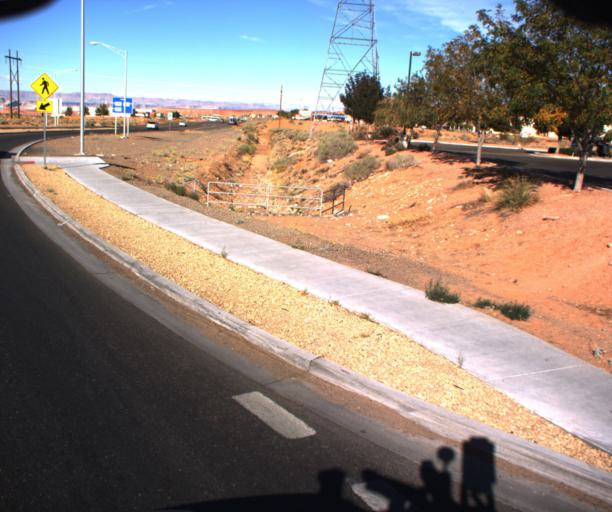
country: US
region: Arizona
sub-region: Coconino County
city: Page
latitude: 36.9050
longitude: -111.4839
